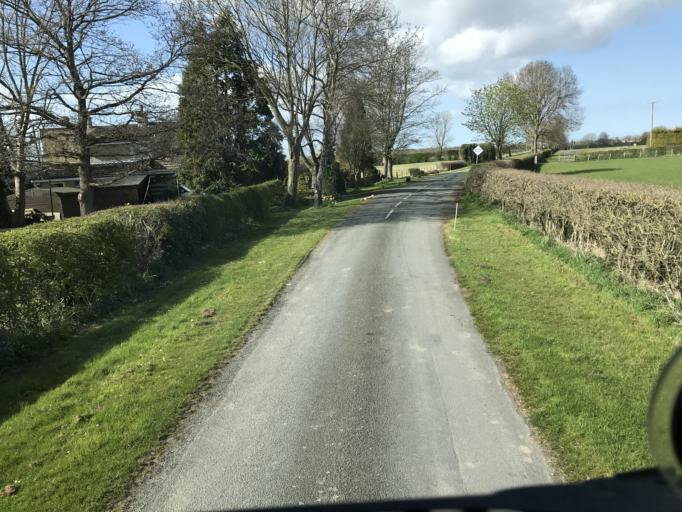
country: GB
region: England
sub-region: Cheshire West and Chester
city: Blacon
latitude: 53.1711
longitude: -2.9471
